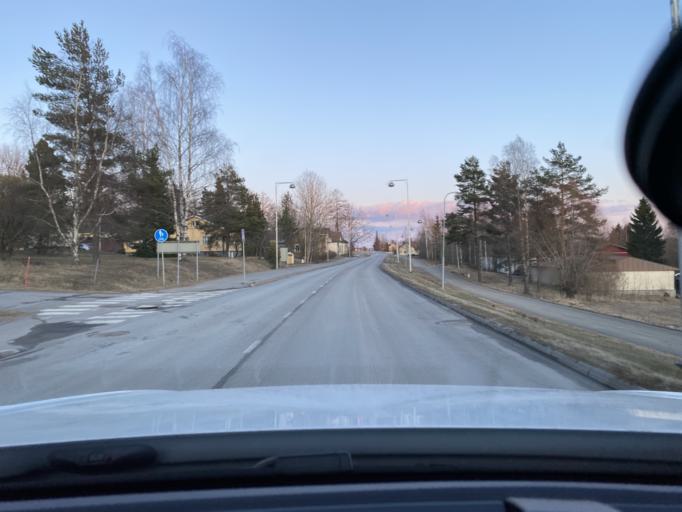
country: FI
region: Pirkanmaa
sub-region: Lounais-Pirkanmaa
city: Punkalaidun
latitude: 61.1091
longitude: 23.1253
